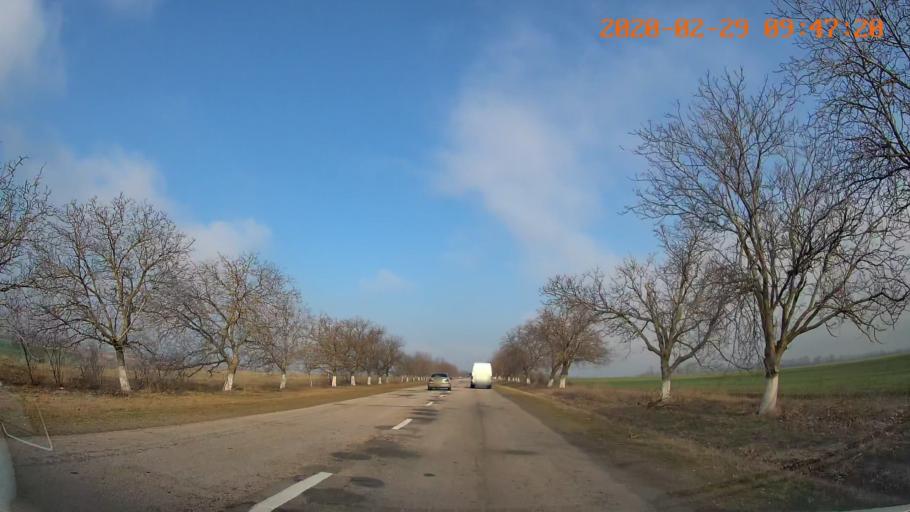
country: MD
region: Telenesti
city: Crasnoe
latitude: 46.6763
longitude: 29.7913
